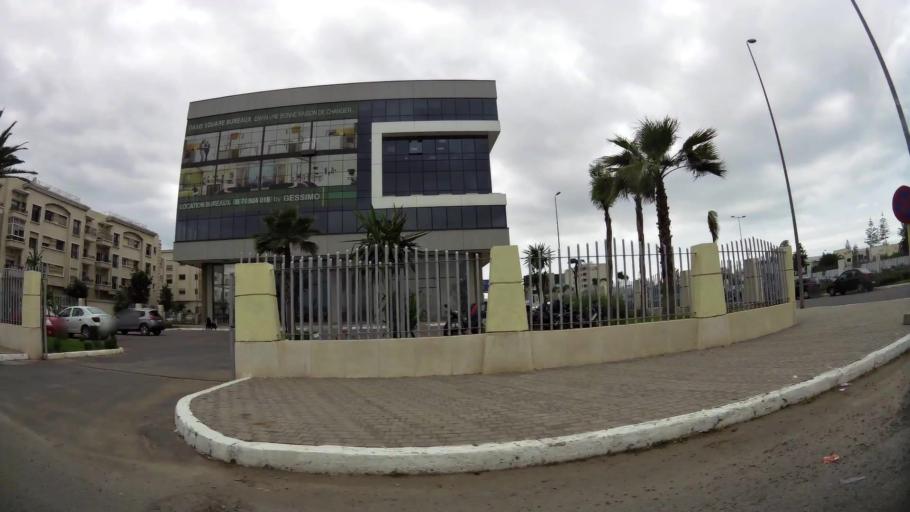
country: MA
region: Grand Casablanca
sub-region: Casablanca
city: Casablanca
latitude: 33.5498
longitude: -7.6388
